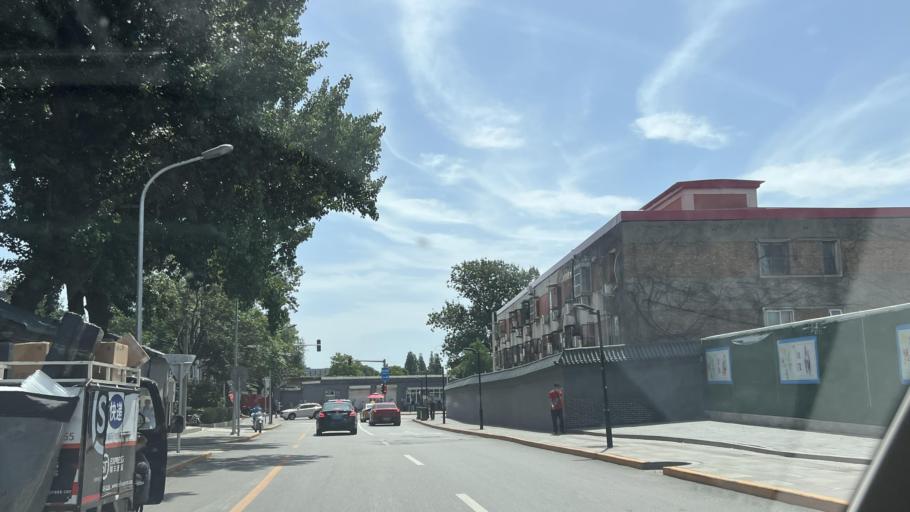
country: CN
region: Beijing
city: Xiangshan
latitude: 39.9915
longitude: 116.2030
